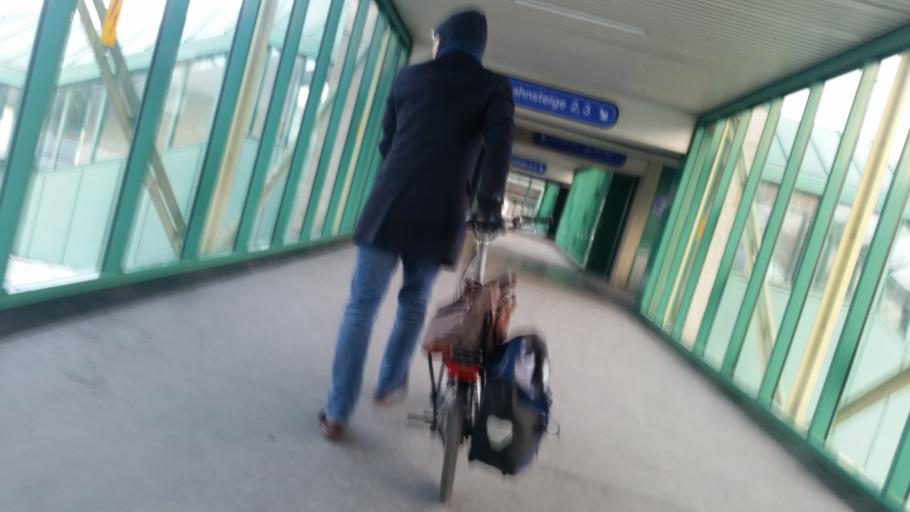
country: AT
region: Vorarlberg
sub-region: Politischer Bezirk Bregenz
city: Bregenz
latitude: 47.5027
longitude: 9.7400
